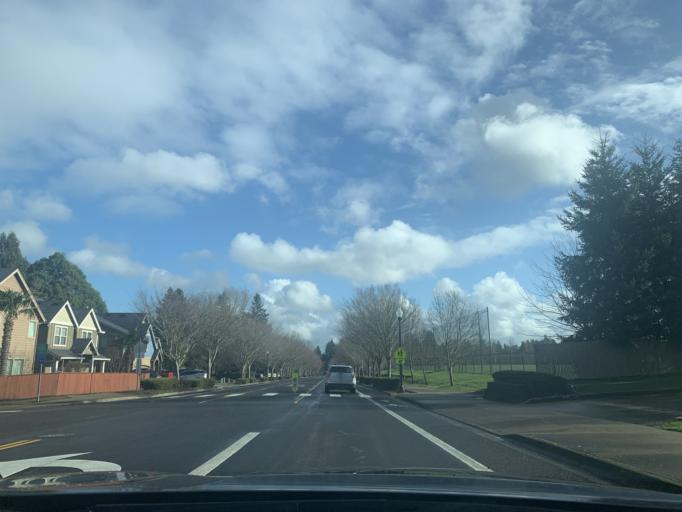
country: US
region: Oregon
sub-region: Washington County
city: Sherwood
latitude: 45.3587
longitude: -122.8540
